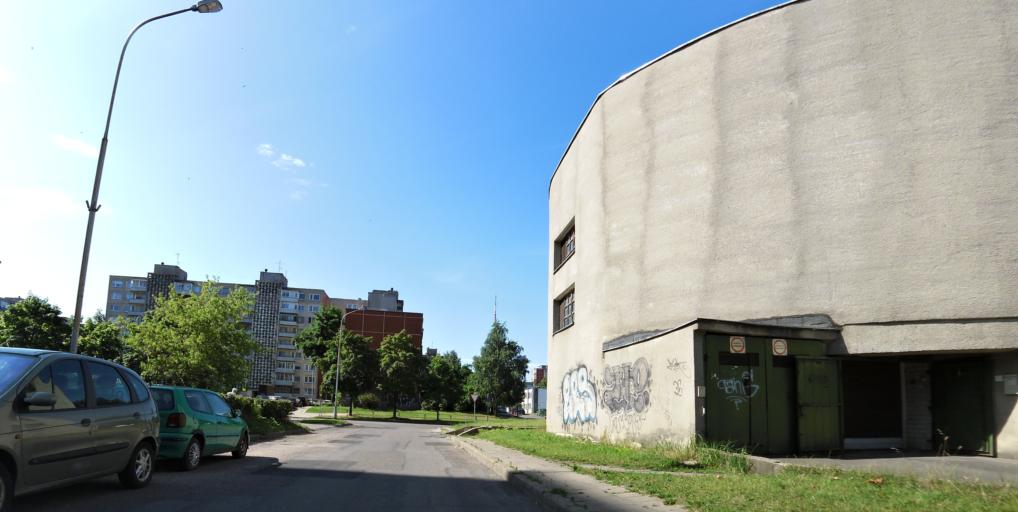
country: LT
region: Vilnius County
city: Justiniskes
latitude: 54.6984
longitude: 25.2238
